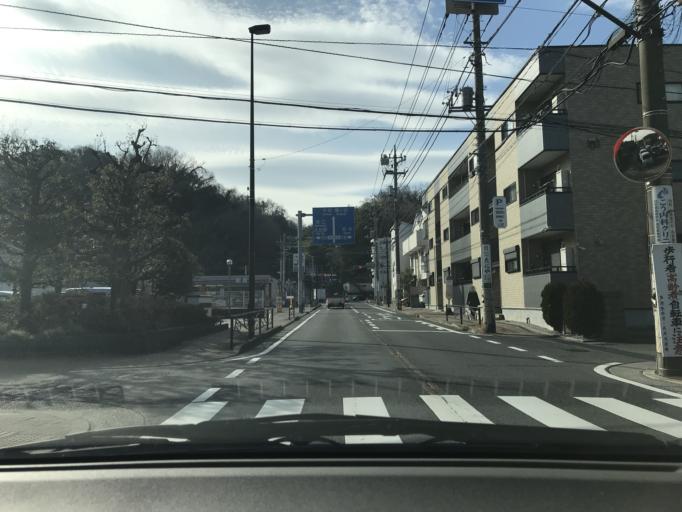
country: JP
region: Tokyo
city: Chofugaoka
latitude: 35.6109
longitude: 139.5761
